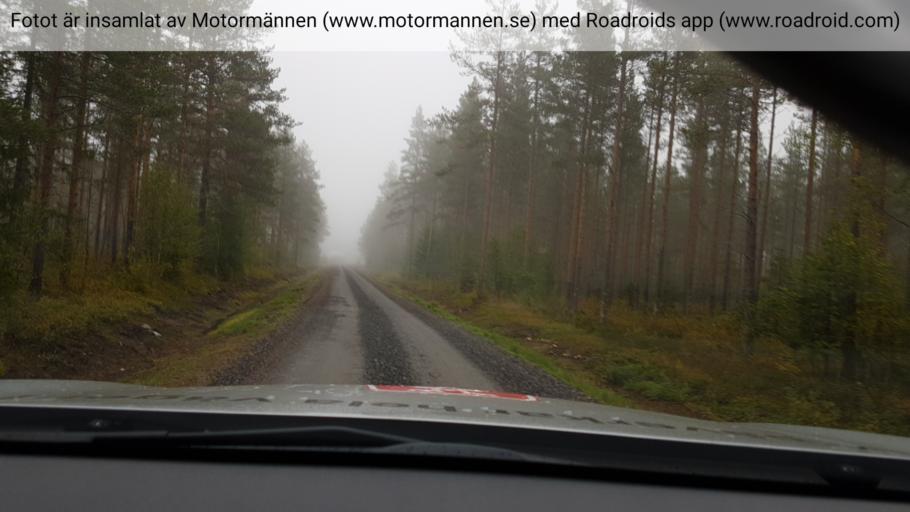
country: SE
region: Vaesterbotten
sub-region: Umea Kommun
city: Ersmark
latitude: 64.1476
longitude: 20.3814
